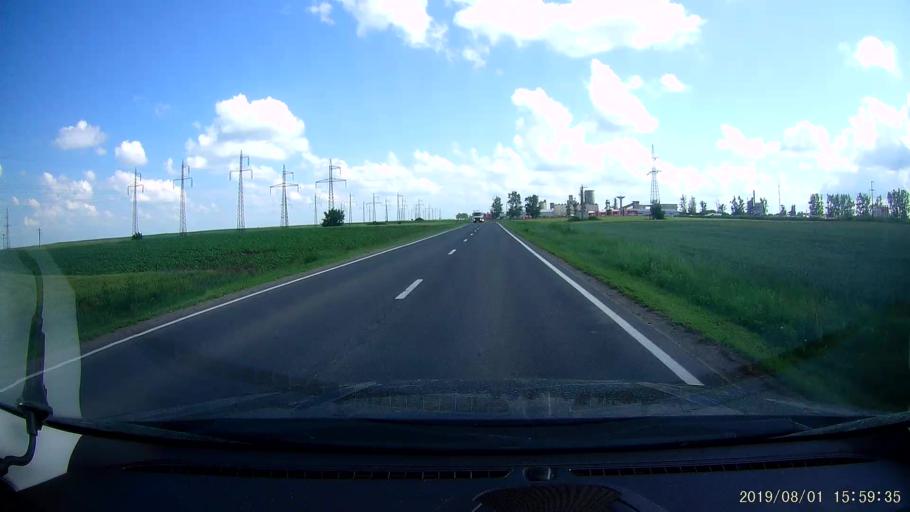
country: RO
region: Ialomita
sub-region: Comuna Slobozia
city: Slobozia
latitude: 44.5456
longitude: 27.3842
